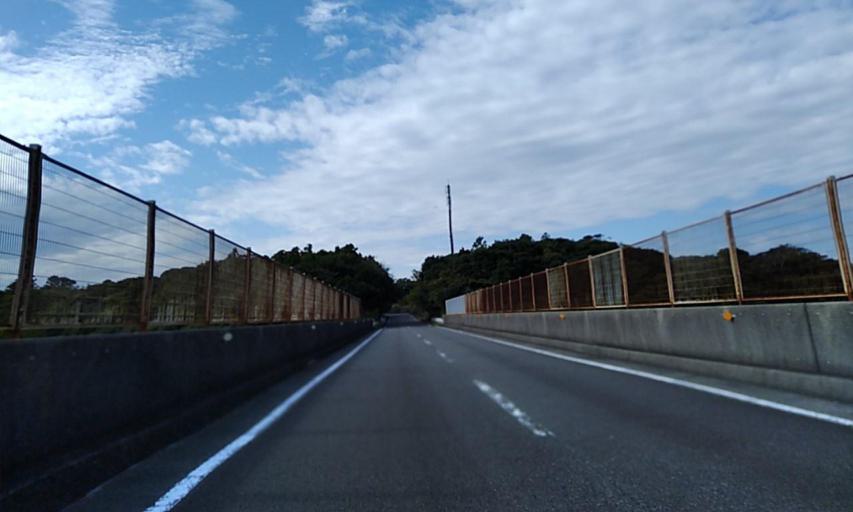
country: JP
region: Wakayama
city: Shingu
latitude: 33.4688
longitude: 135.8526
